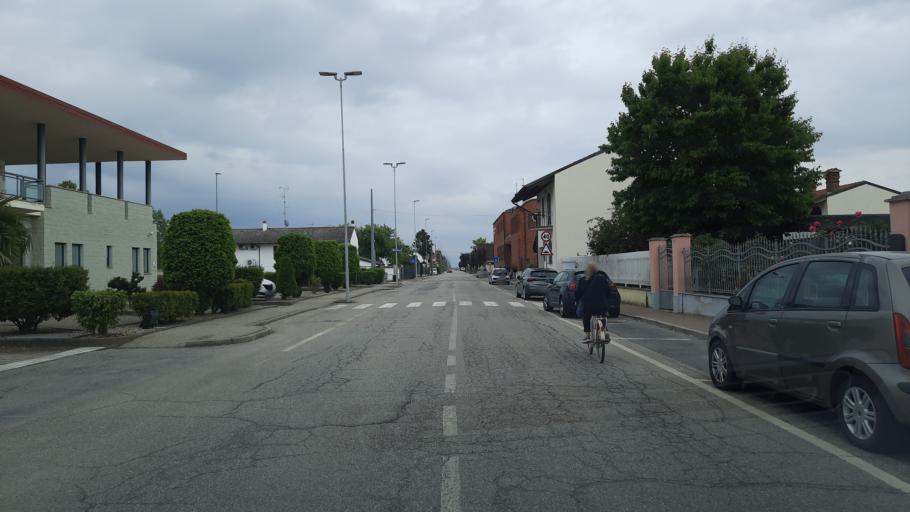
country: IT
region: Lombardy
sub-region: Provincia di Pavia
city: Robbio
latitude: 45.2870
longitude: 8.5957
